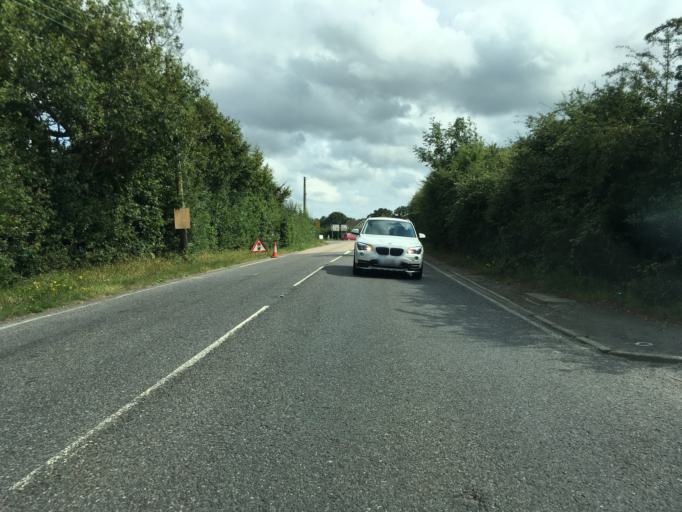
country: GB
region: England
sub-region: Kent
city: Tenterden
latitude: 51.0971
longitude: 0.6882
